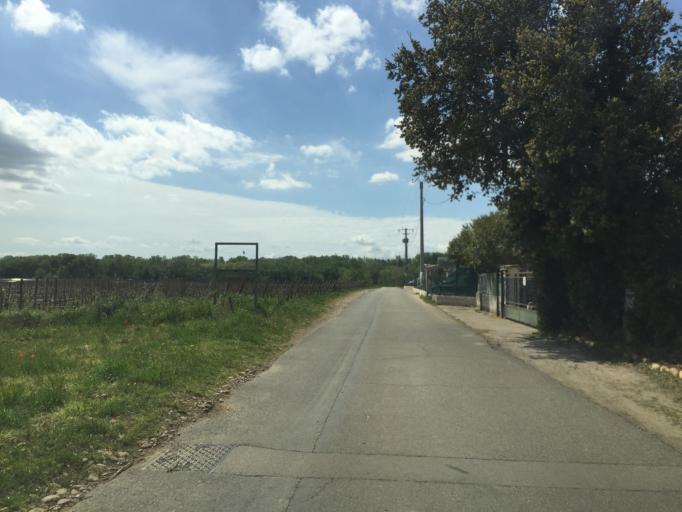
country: FR
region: Provence-Alpes-Cote d'Azur
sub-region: Departement du Vaucluse
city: Chateauneuf-du-Pape
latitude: 44.0454
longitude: 4.8286
